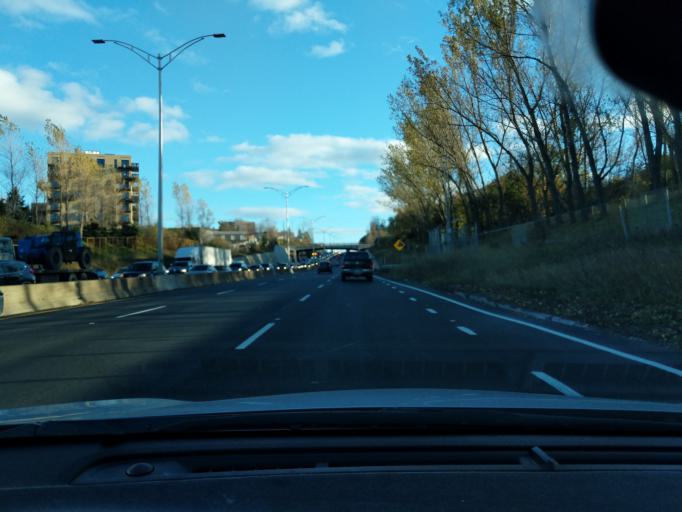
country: CA
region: Quebec
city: L'Ancienne-Lorette
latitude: 46.7794
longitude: -71.3080
